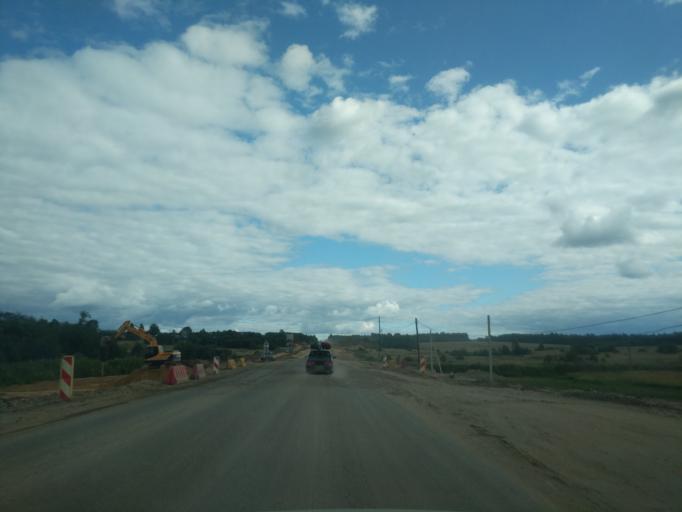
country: RU
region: Kostroma
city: Sudislavl'
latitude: 57.8766
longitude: 41.7300
